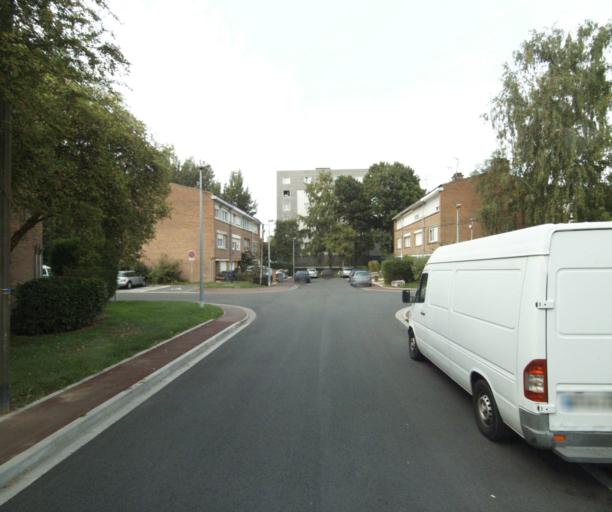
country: FR
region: Nord-Pas-de-Calais
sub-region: Departement du Nord
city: Loos
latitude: 50.6054
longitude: 3.0121
